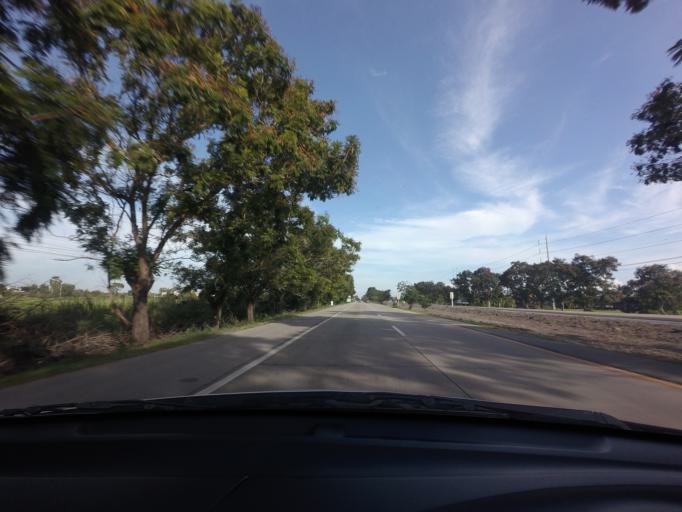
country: TH
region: Phra Nakhon Si Ayutthaya
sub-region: Amphoe Bang Sai
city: Bang Sai
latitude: 14.2537
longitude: 100.2606
